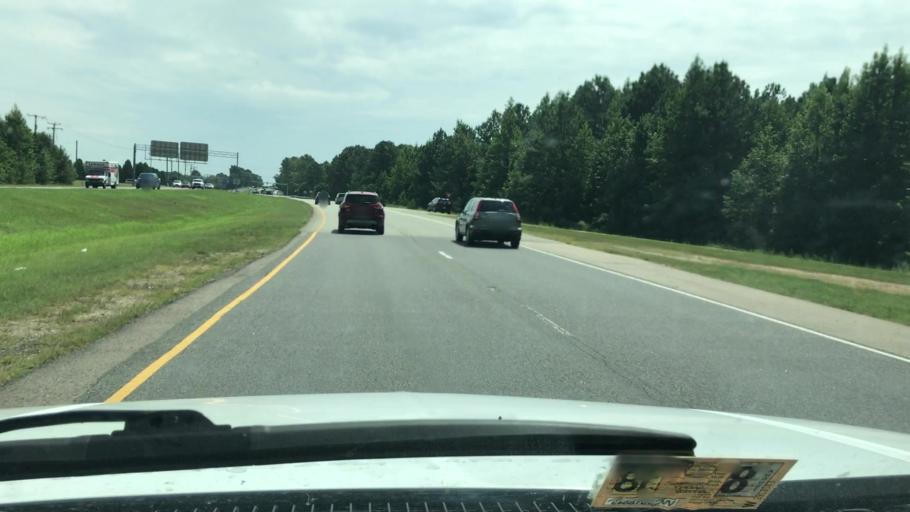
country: US
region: Virginia
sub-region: Chesterfield County
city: Brandermill
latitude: 37.5093
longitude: -77.6823
